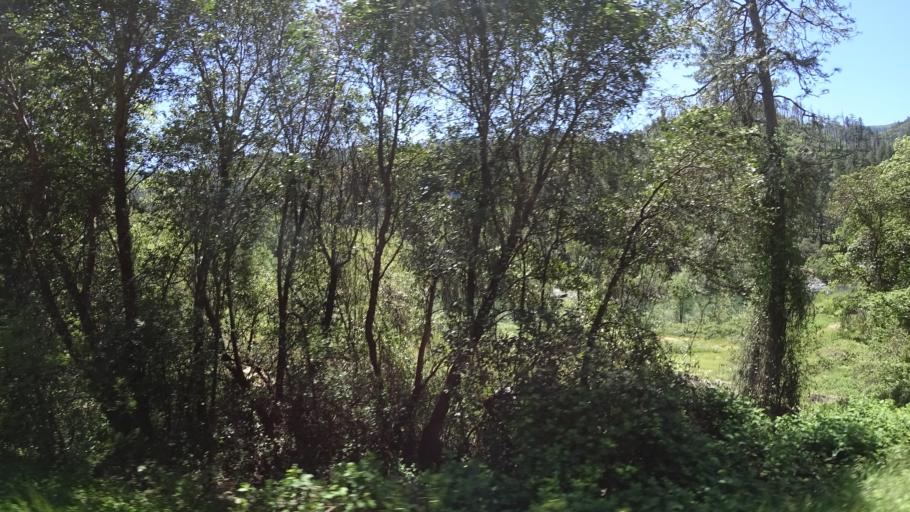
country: US
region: California
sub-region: Trinity County
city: Hayfork
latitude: 40.7472
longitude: -123.2703
